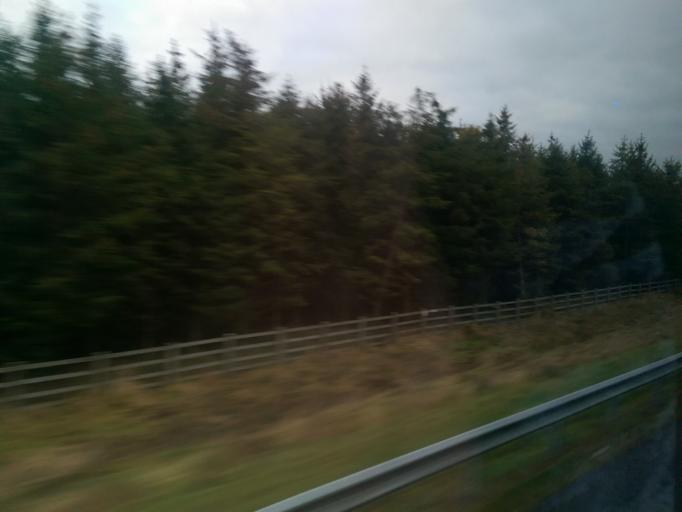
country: IE
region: Connaught
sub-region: County Galway
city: Ballinasloe
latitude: 53.2914
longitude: -8.3720
